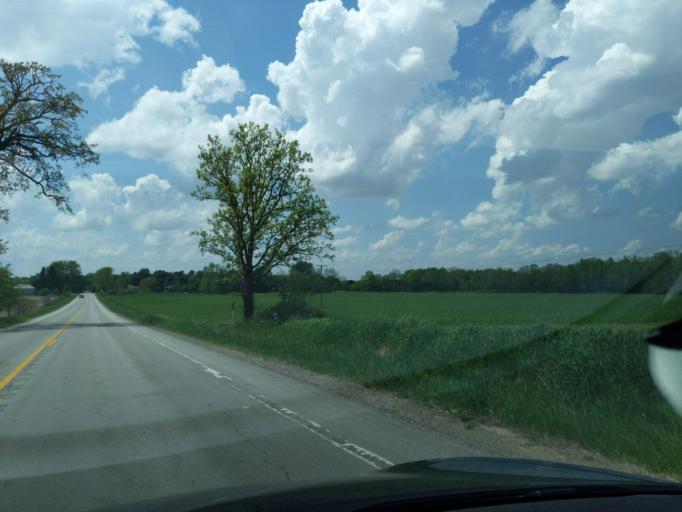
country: US
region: Michigan
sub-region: Ingham County
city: Stockbridge
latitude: 42.5521
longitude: -84.2225
